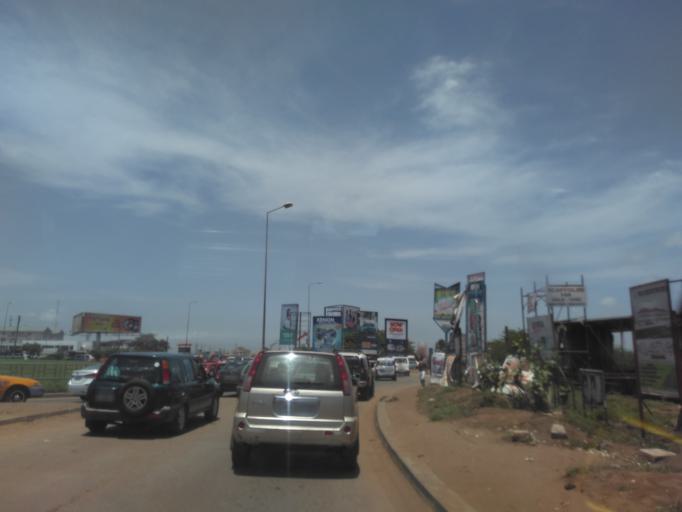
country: GH
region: Greater Accra
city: Tema
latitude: 5.6844
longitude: -0.0152
